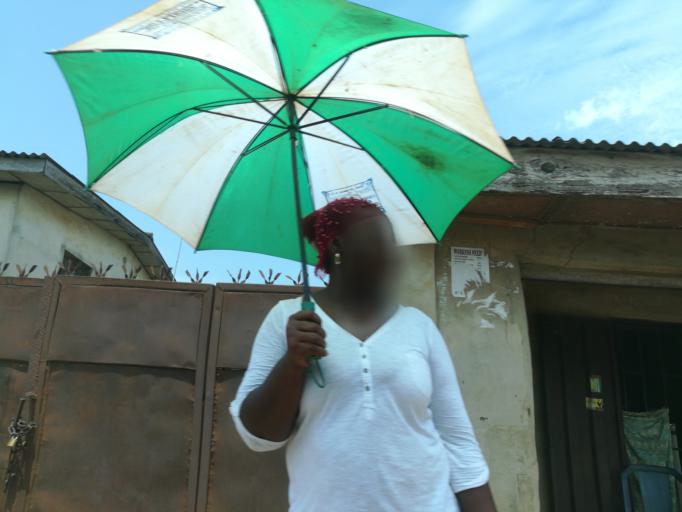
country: NG
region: Lagos
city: Ikorodu
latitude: 6.6232
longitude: 3.4941
